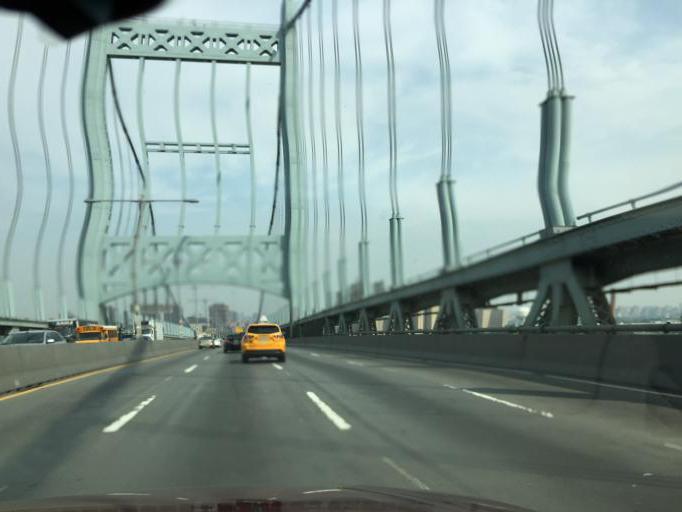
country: US
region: New York
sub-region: New York County
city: Manhattan
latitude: 40.7806
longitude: -73.9273
